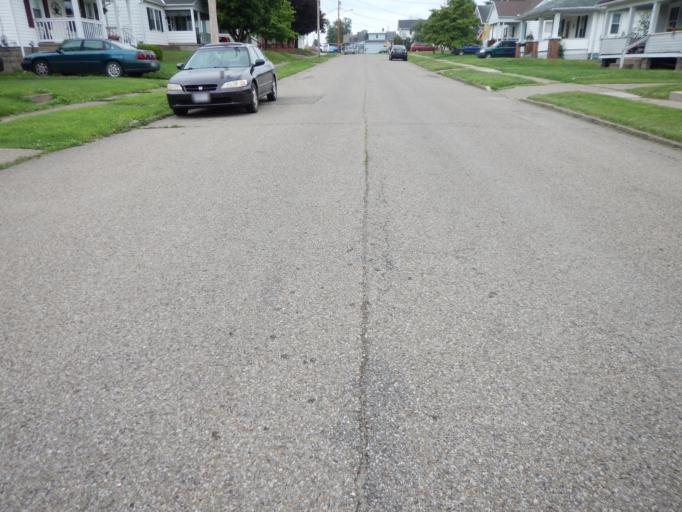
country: US
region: Ohio
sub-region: Muskingum County
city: Zanesville
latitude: 39.9203
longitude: -82.0196
